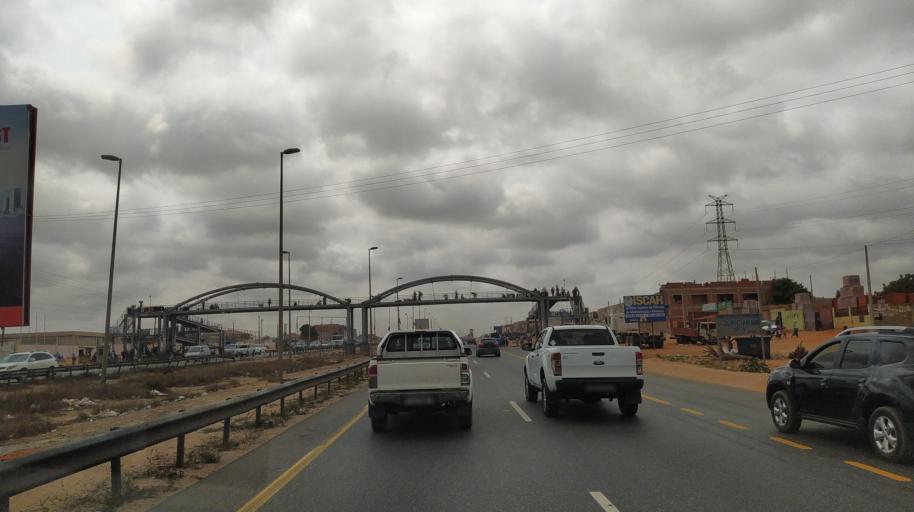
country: AO
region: Luanda
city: Luanda
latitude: -8.9731
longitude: 13.3050
